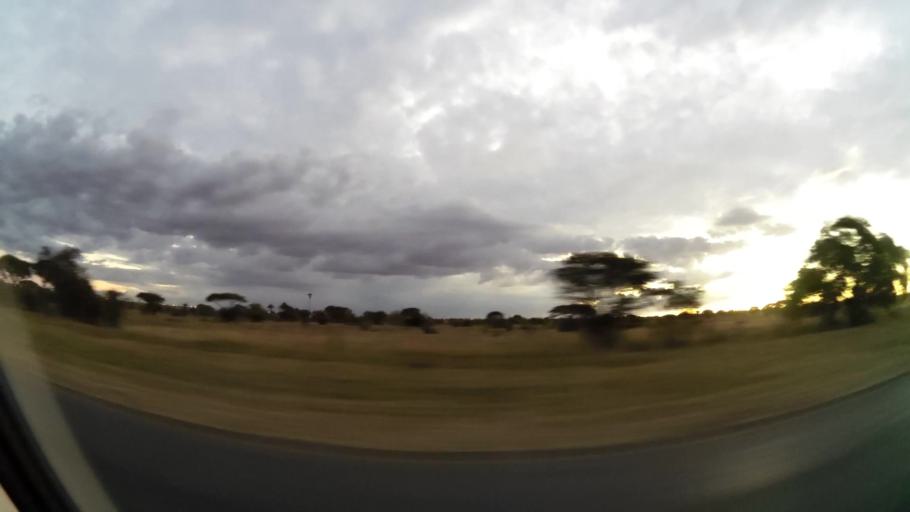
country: ZA
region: Limpopo
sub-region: Capricorn District Municipality
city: Polokwane
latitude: -23.8478
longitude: 29.4282
